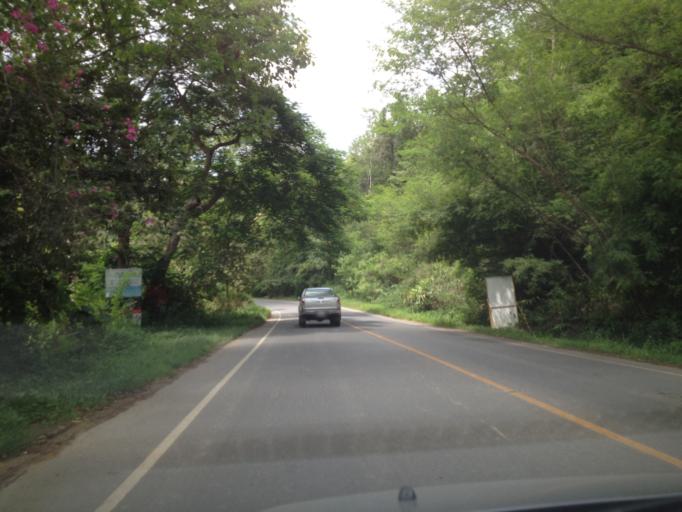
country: TH
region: Chiang Mai
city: Hang Dong
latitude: 18.7356
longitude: 98.8927
